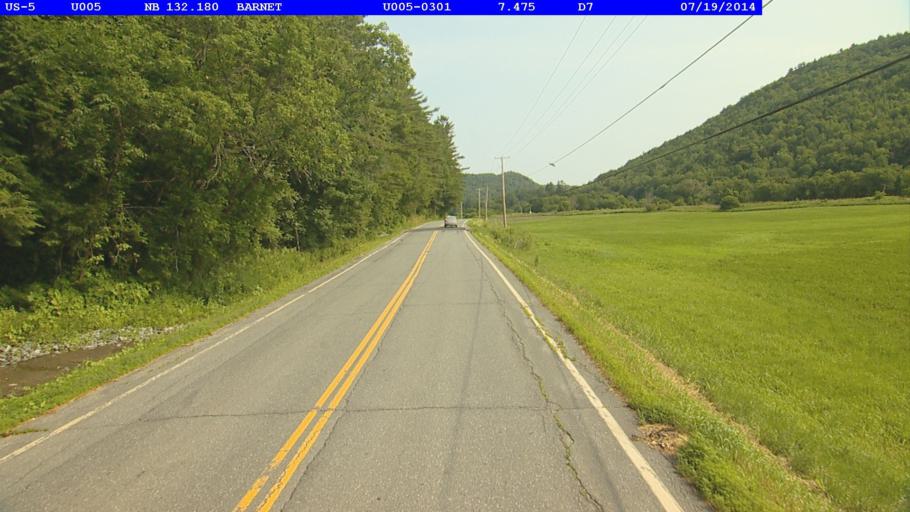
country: US
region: Vermont
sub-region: Caledonia County
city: Saint Johnsbury
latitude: 44.3508
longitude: -72.0468
